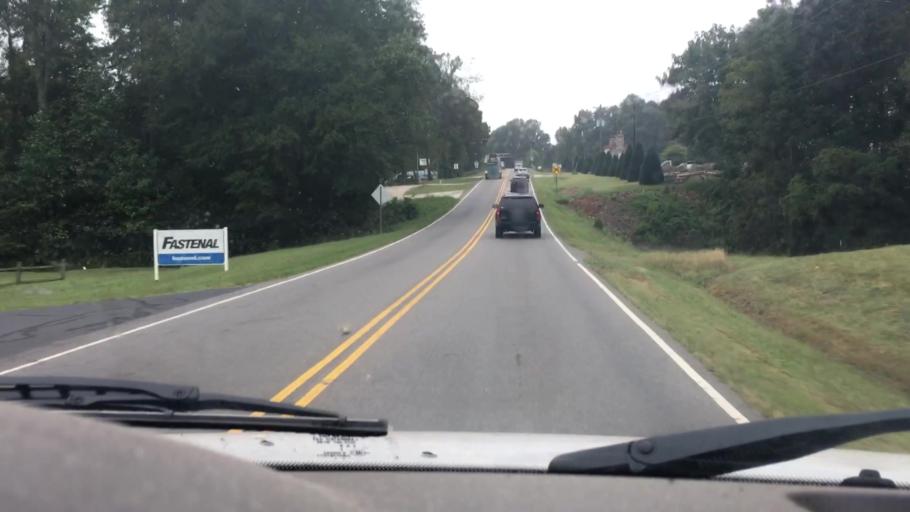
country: US
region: North Carolina
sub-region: Iredell County
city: Mooresville
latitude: 35.6076
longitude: -80.8024
